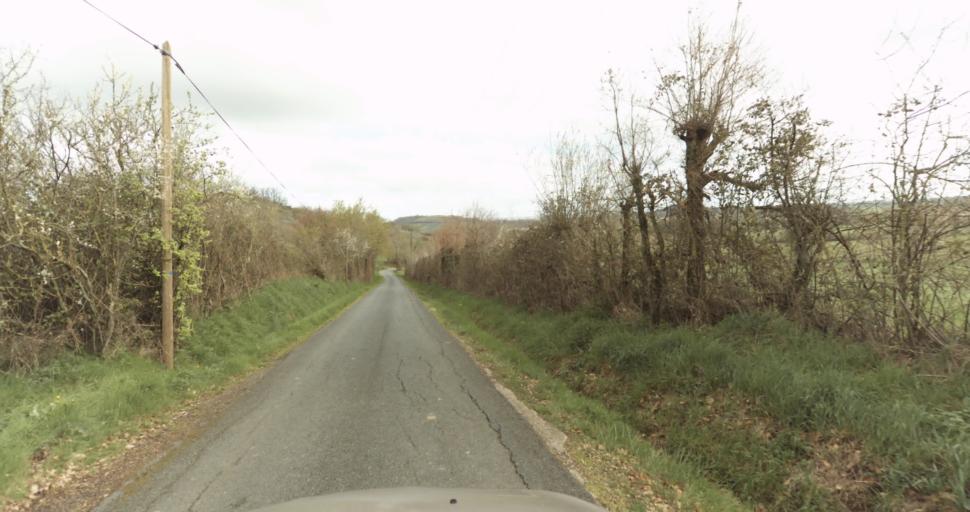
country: FR
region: Midi-Pyrenees
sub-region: Departement du Tarn
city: Puygouzon
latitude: 43.8751
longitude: 2.1942
